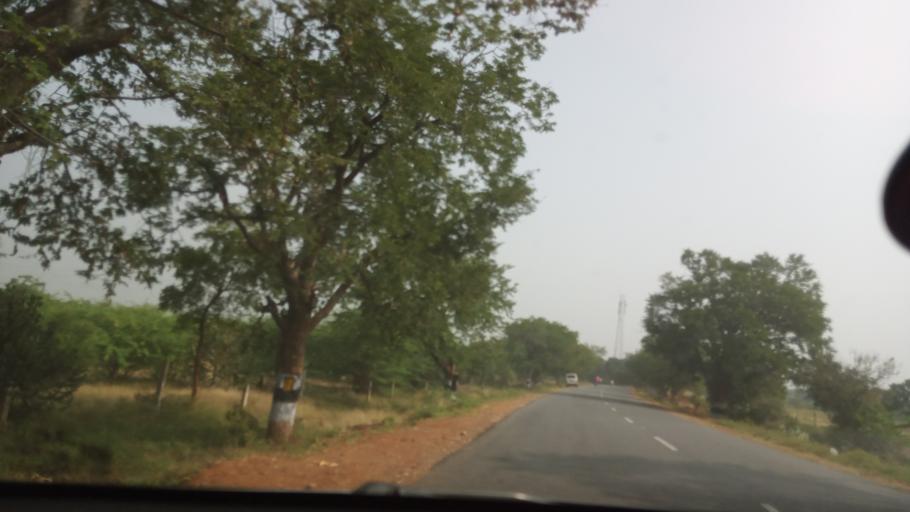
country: IN
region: Tamil Nadu
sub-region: Erode
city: Sathyamangalam
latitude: 11.4339
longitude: 77.2028
